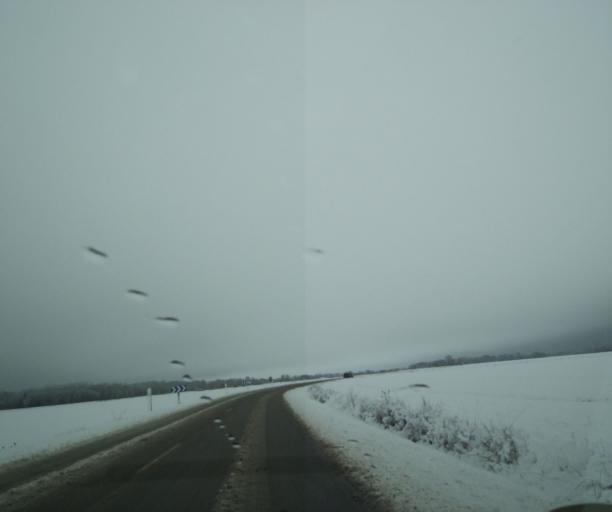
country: FR
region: Champagne-Ardenne
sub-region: Departement de la Haute-Marne
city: Wassy
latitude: 48.5326
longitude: 4.9248
